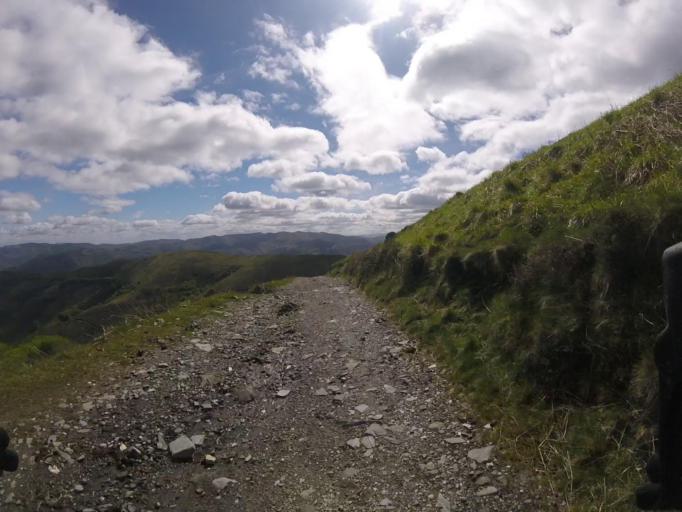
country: ES
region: Navarre
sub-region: Provincia de Navarra
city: Arano
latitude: 43.1752
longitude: -1.9196
